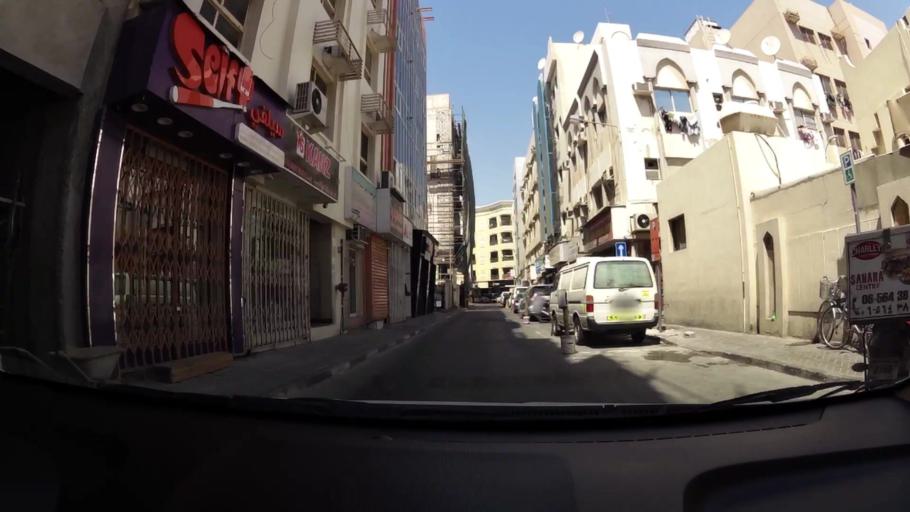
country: AE
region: Ash Shariqah
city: Sharjah
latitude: 25.2768
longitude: 55.3072
